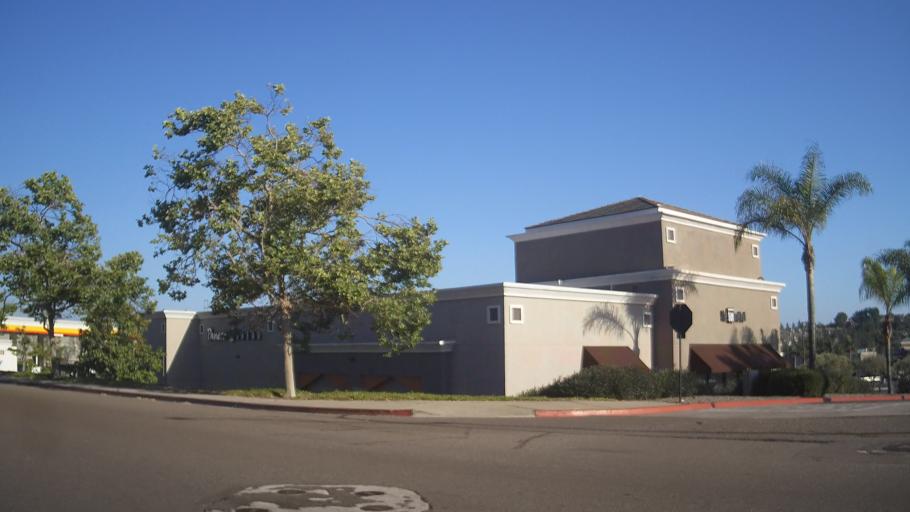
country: US
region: California
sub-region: San Diego County
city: Poway
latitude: 32.9857
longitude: -117.0769
